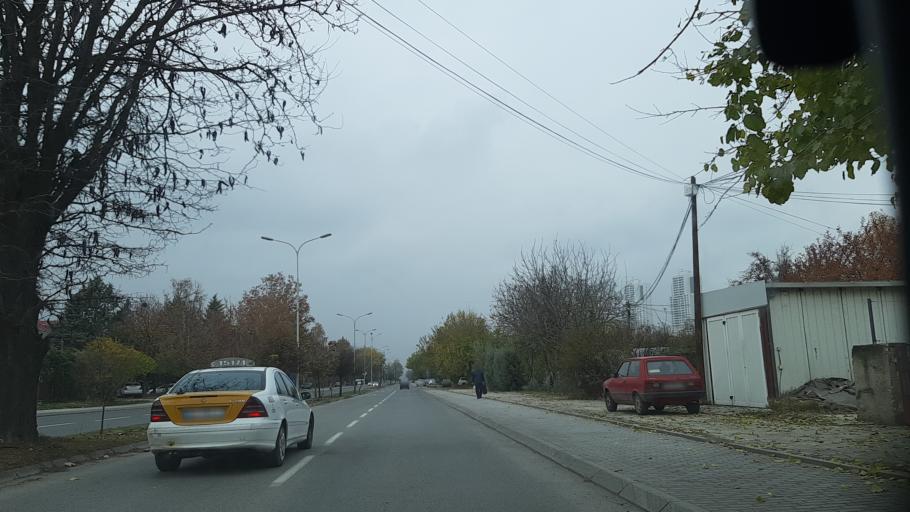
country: MK
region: Kisela Voda
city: Usje
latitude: 41.9732
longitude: 21.4736
